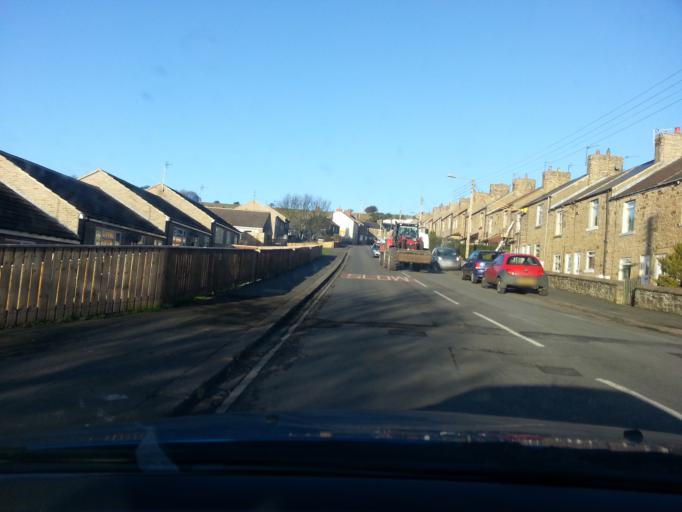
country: GB
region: England
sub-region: County Durham
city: Crook
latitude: 54.7315
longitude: -1.7509
